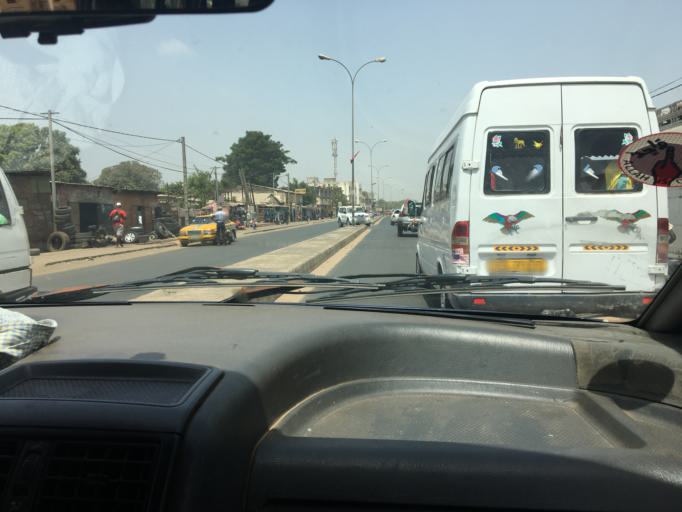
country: GM
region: Western
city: Abuko
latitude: 13.4093
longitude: -16.6683
